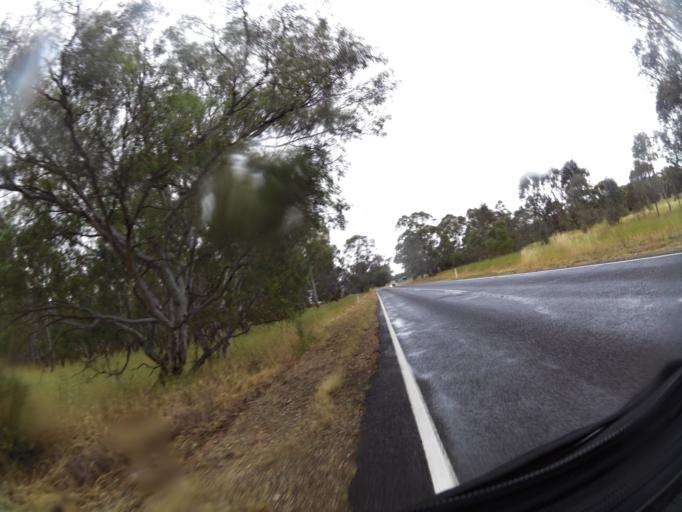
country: AU
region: Victoria
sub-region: Mount Alexander
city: Castlemaine
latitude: -37.1444
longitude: 144.0407
